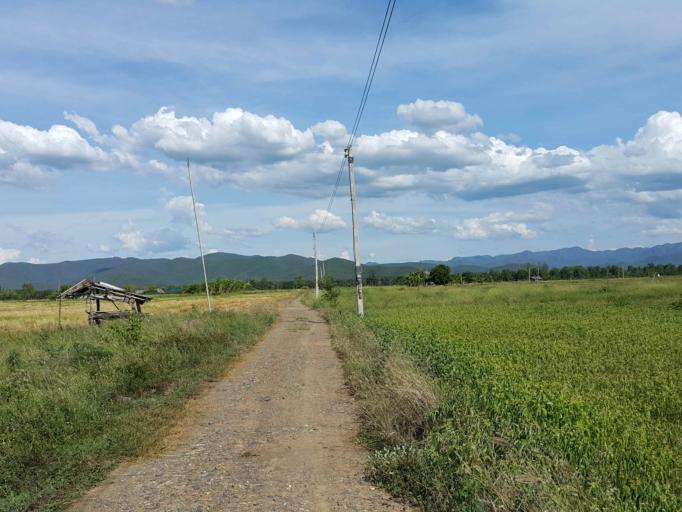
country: TH
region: Chiang Mai
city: San Kamphaeng
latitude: 18.8001
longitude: 99.1525
